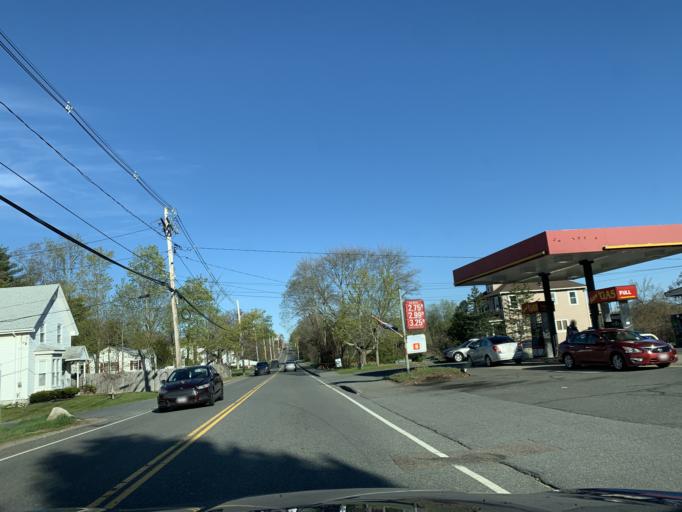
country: US
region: Massachusetts
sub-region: Norfolk County
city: Stoughton
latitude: 42.1290
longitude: -71.1199
